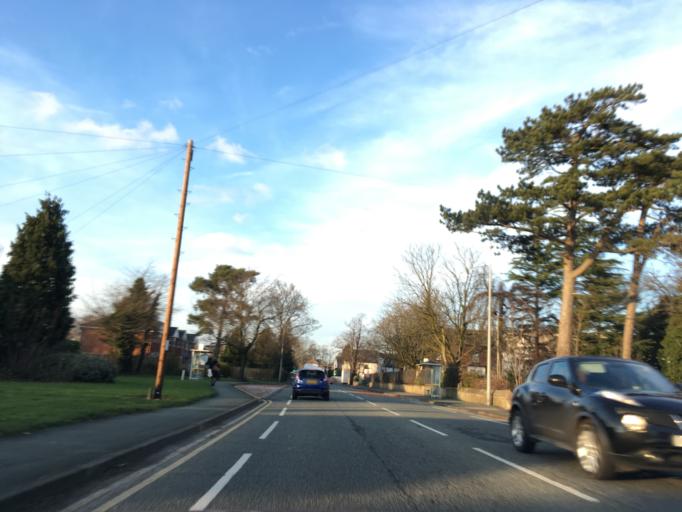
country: GB
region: England
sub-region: Cheshire East
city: Wilmslow
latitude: 53.3527
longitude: -2.2161
